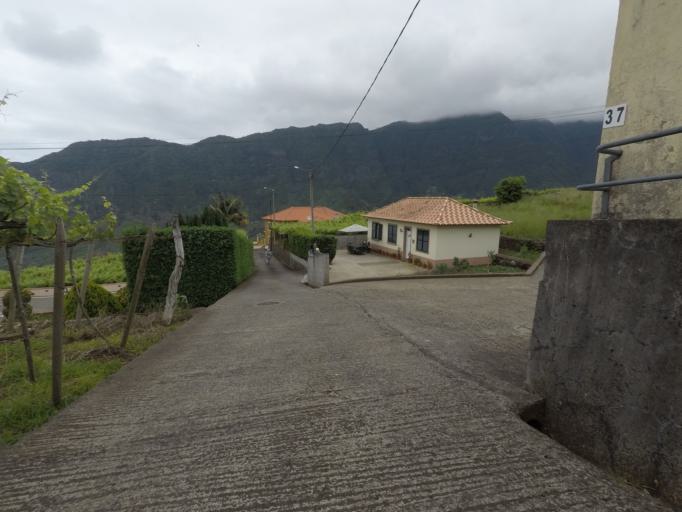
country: PT
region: Madeira
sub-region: Sao Vicente
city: Sao Vicente
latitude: 32.7859
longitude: -17.0424
